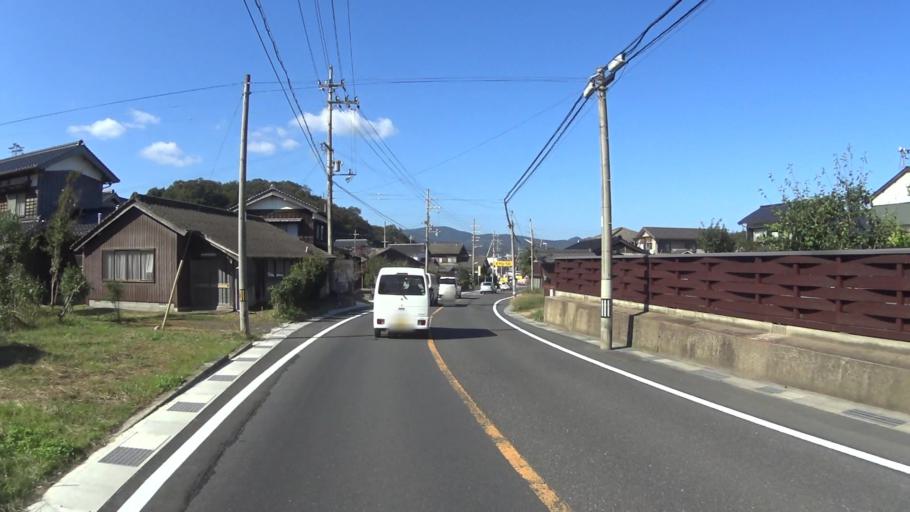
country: JP
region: Kyoto
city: Miyazu
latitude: 35.6822
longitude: 135.0461
